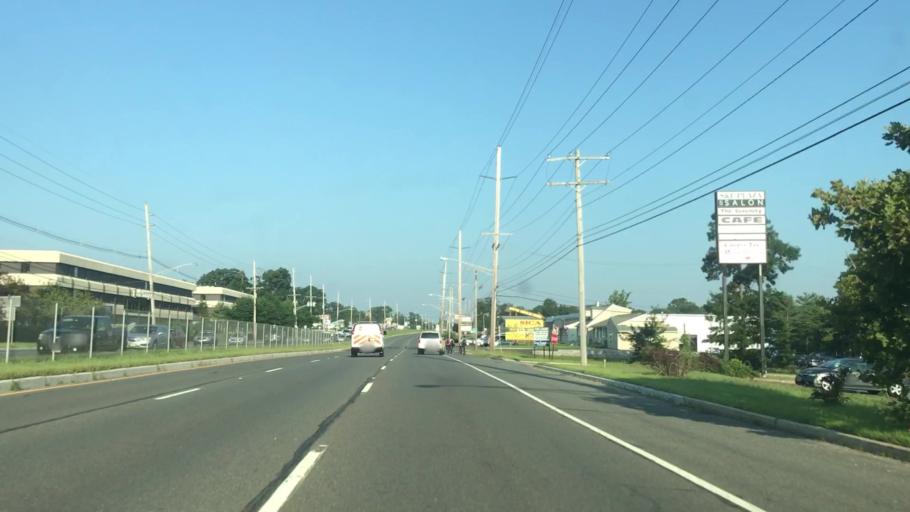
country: US
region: New Jersey
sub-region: Ocean County
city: Island Heights
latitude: 39.9510
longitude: -74.1416
